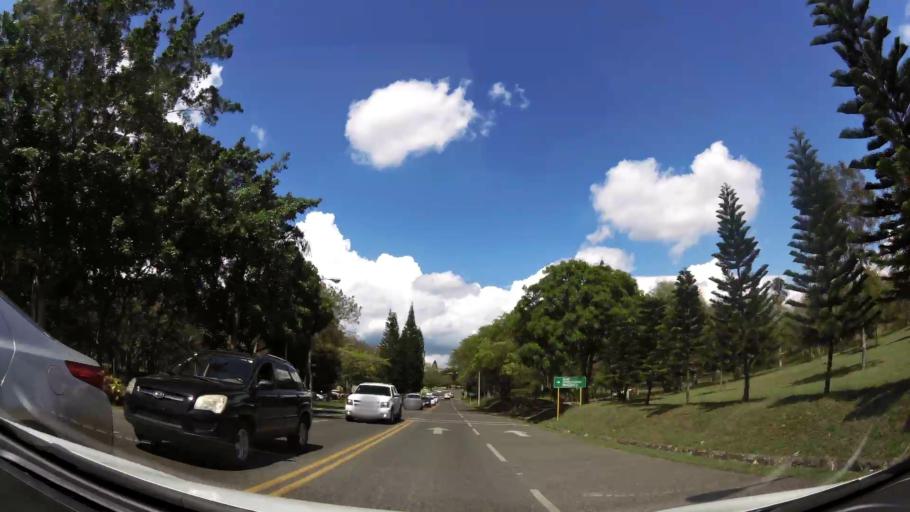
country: DO
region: Santiago
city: Santiago de los Caballeros
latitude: 19.4453
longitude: -70.6854
